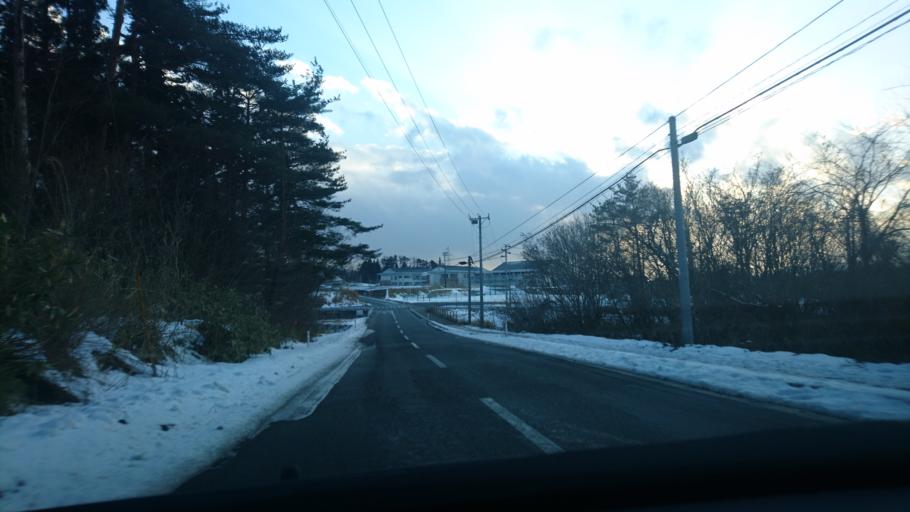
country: JP
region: Iwate
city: Ichinoseki
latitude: 39.0074
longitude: 141.3331
